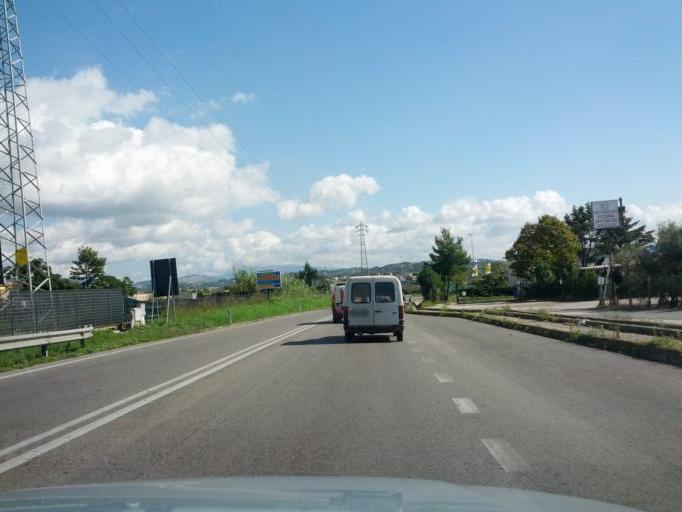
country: IT
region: Latium
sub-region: Provincia di Latina
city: Penitro
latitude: 41.2685
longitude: 13.6746
